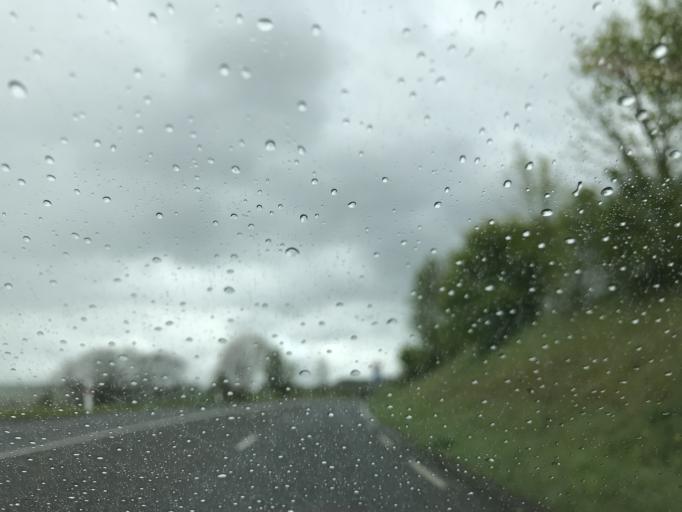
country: FR
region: Auvergne
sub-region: Departement du Puy-de-Dome
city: Billom
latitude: 45.7169
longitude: 3.3874
